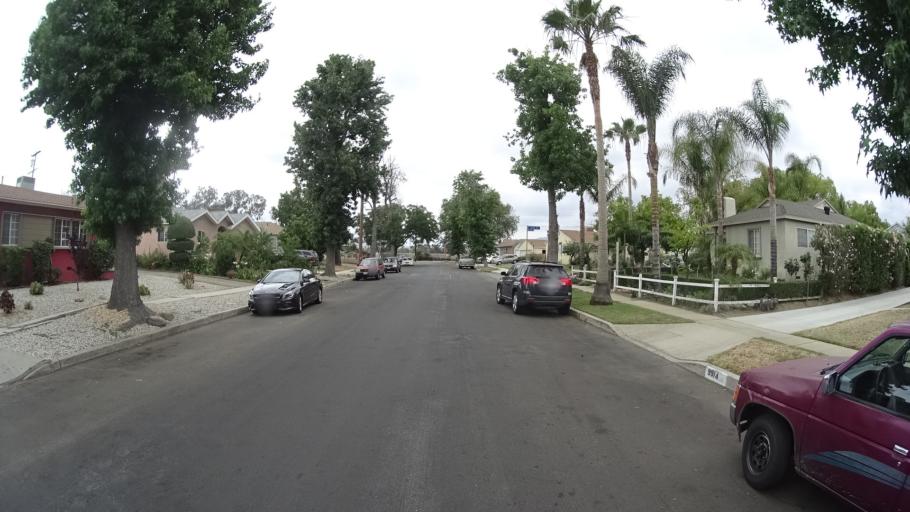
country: US
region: California
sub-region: Los Angeles County
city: San Fernando
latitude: 34.2504
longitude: -118.4491
